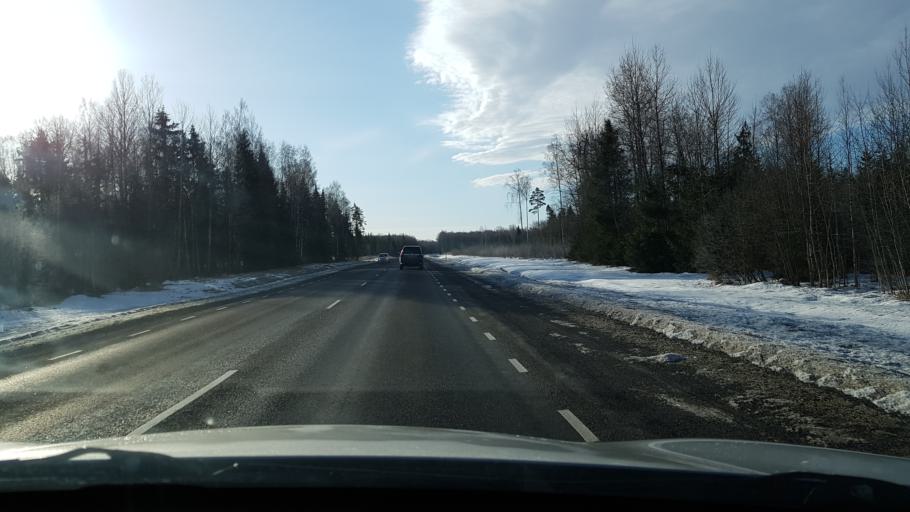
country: EE
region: Viljandimaa
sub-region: Vohma linn
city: Vohma
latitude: 58.6100
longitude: 25.5718
